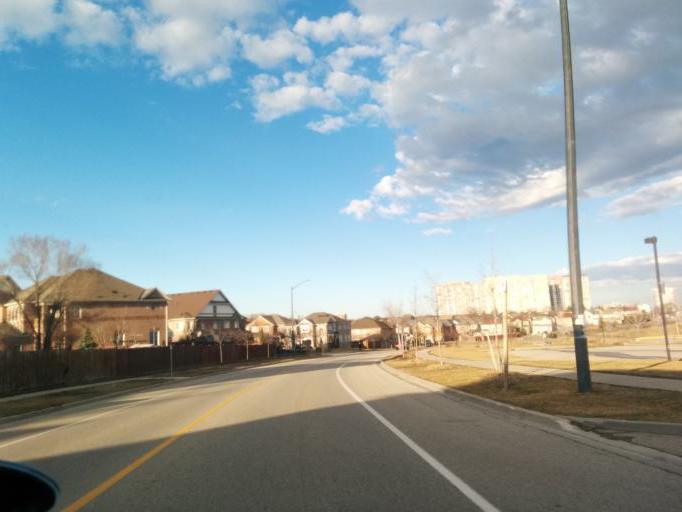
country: CA
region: Ontario
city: Mississauga
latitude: 43.5739
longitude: -79.6311
